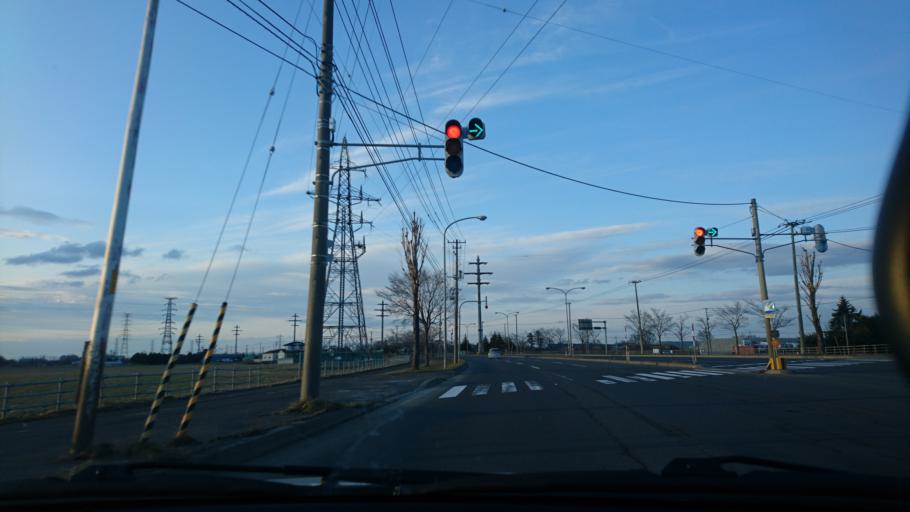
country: JP
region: Hokkaido
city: Sapporo
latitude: 43.1282
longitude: 141.4183
